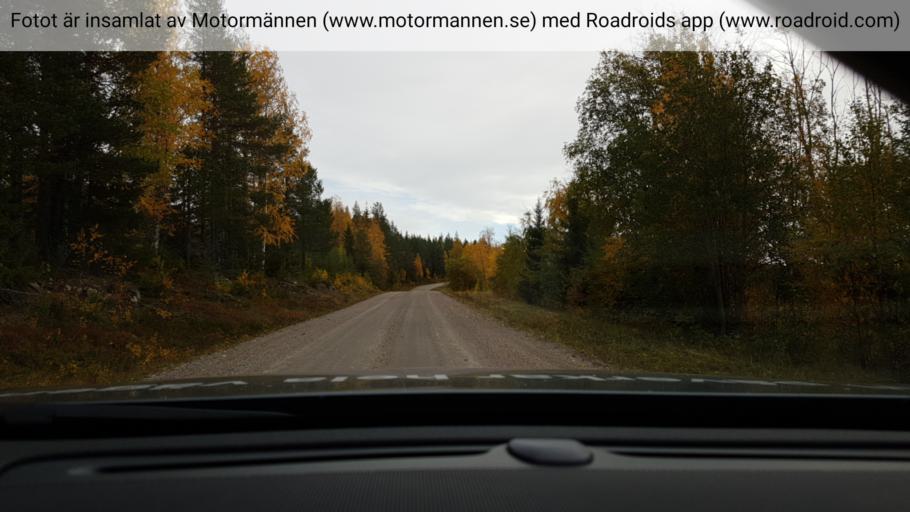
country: SE
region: Norrbotten
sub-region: Overkalix Kommun
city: OEverkalix
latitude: 66.2646
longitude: 23.0204
